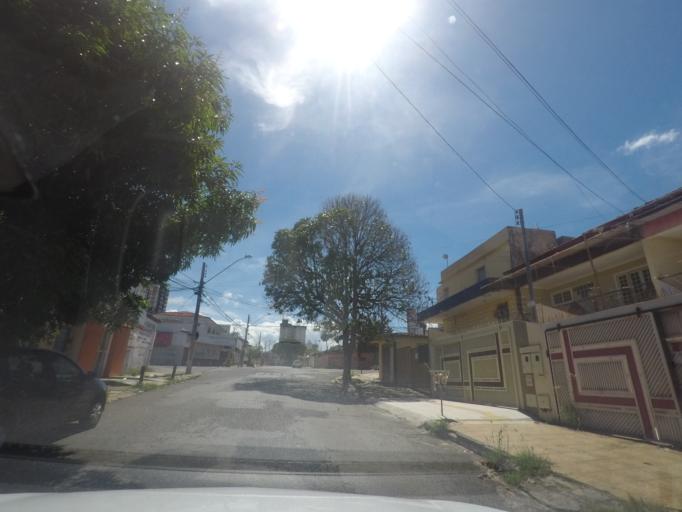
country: BR
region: Goias
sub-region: Goiania
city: Goiania
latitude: -16.6739
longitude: -49.2749
